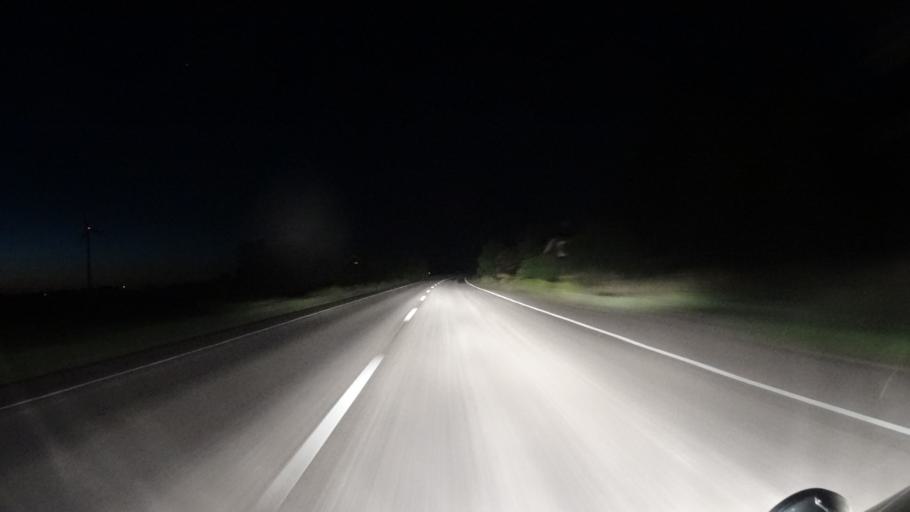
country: SE
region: OEstergoetland
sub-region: Vadstena Kommun
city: Herrestad
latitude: 58.2972
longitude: 14.8006
